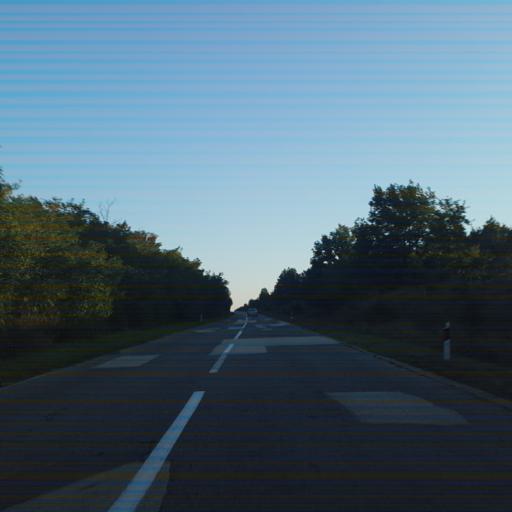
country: RS
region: Central Serbia
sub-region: Borski Okrug
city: Negotin
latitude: 44.1568
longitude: 22.3598
